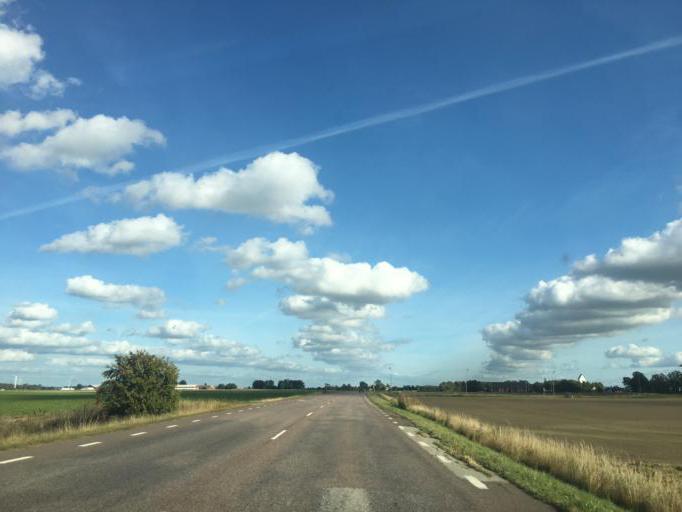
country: SE
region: Skane
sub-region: Kavlinge Kommun
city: Kaevlinge
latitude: 55.7967
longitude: 13.1871
